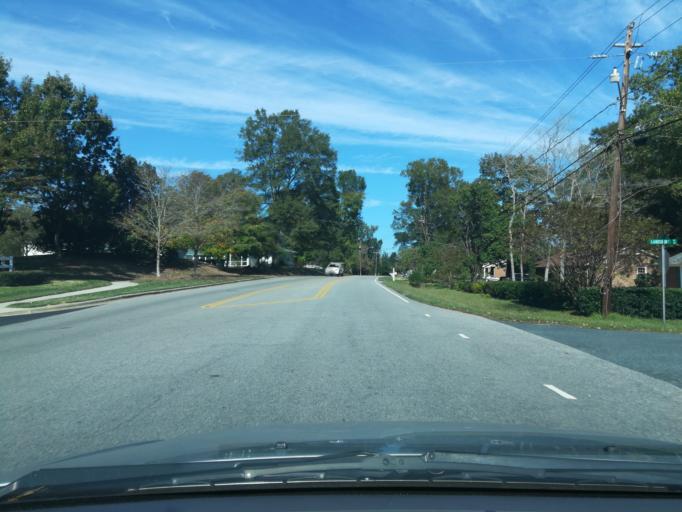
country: US
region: North Carolina
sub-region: Durham County
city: Durham
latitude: 35.9671
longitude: -78.9765
